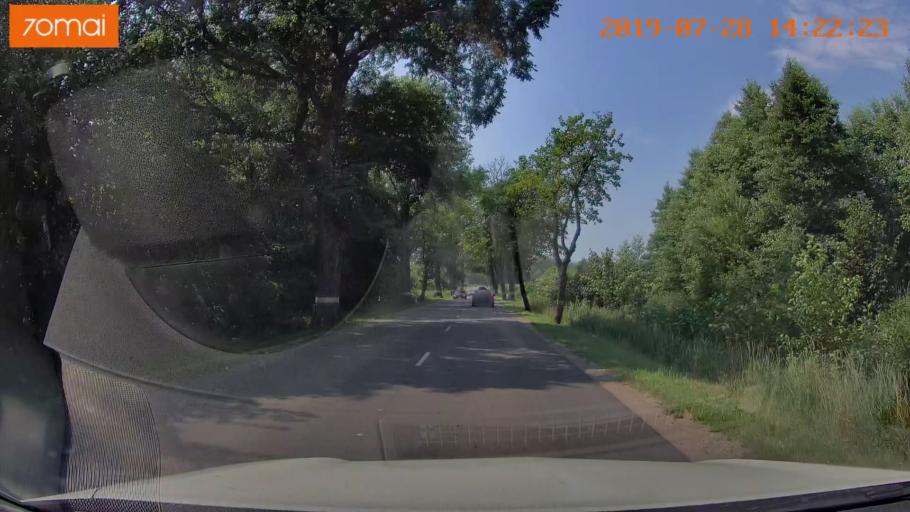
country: RU
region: Kaliningrad
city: Volochayevskoye
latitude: 54.8147
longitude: 20.1824
